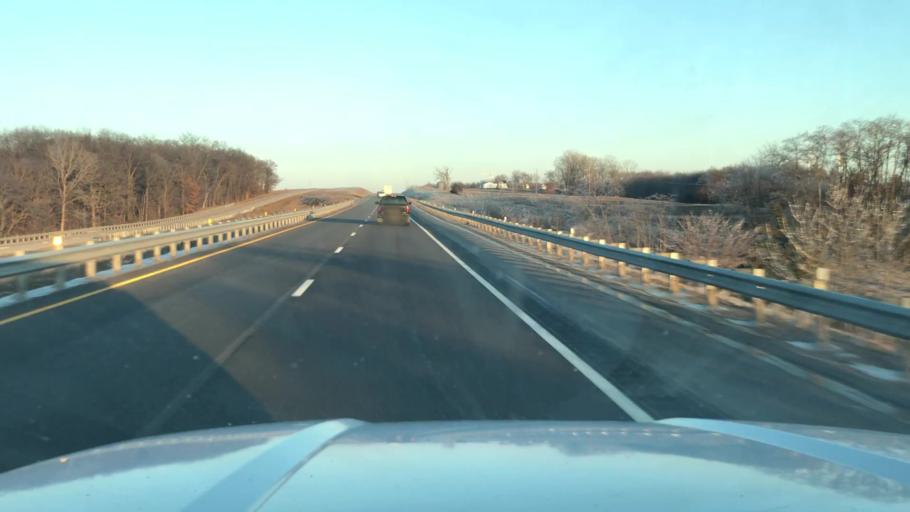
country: US
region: Missouri
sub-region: DeKalb County
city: Maysville
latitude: 39.7620
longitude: -94.4703
